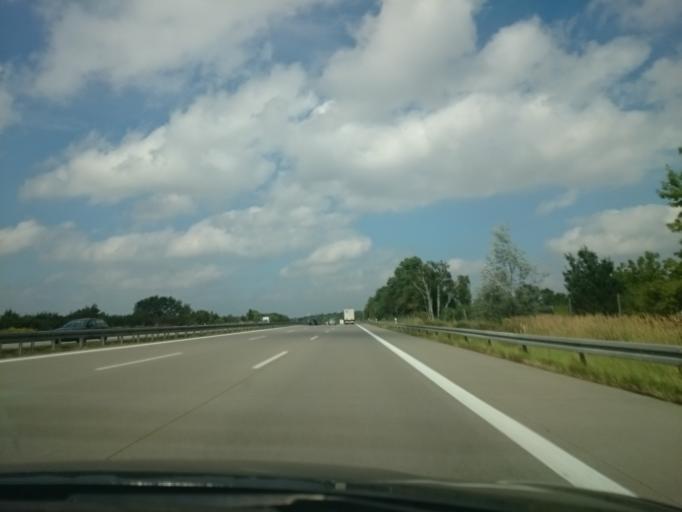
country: DE
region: Berlin
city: Hellersdorf
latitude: 52.5747
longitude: 13.6428
